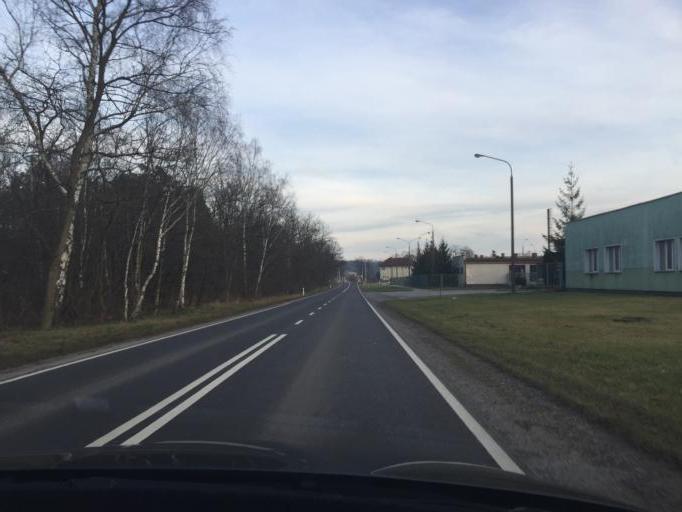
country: PL
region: Lubusz
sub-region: Powiat zielonogorski
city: Nowogrod Bobrzanski
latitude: 51.7980
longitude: 15.2242
